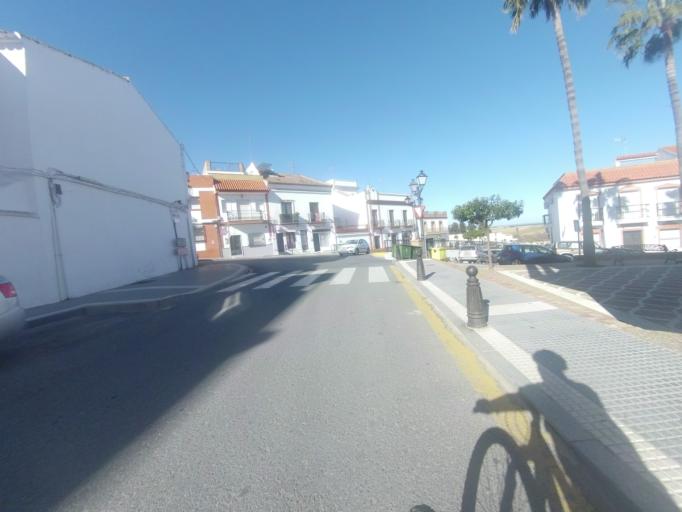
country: ES
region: Andalusia
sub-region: Provincia de Huelva
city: Palos de la Frontera
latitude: 37.2298
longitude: -6.8913
